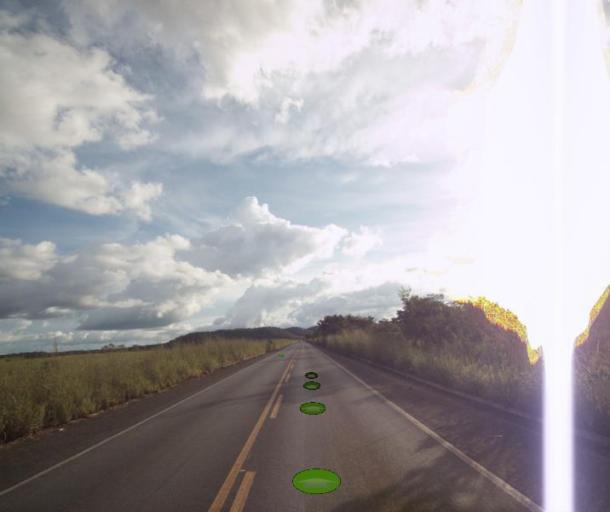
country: BR
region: Goias
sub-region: Niquelandia
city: Niquelandia
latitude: -14.5386
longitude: -48.5439
